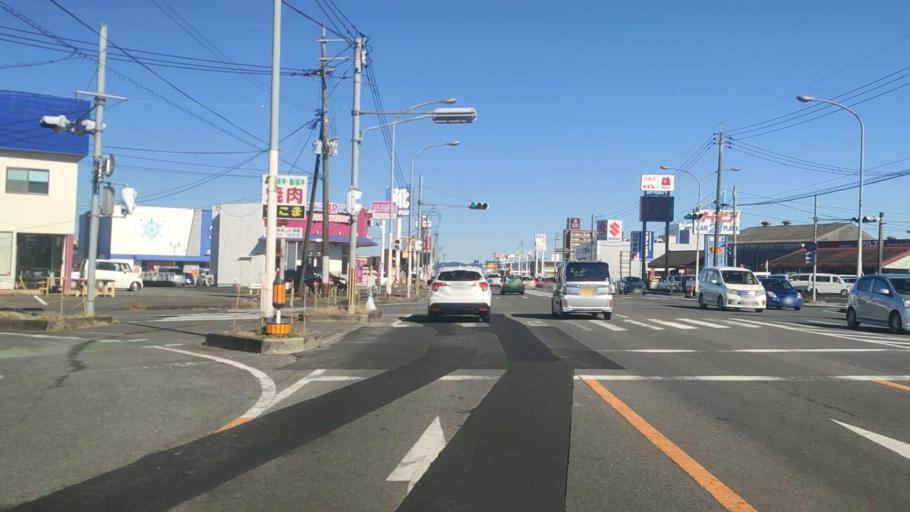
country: JP
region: Miyazaki
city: Miyakonojo
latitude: 31.7549
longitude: 131.0814
